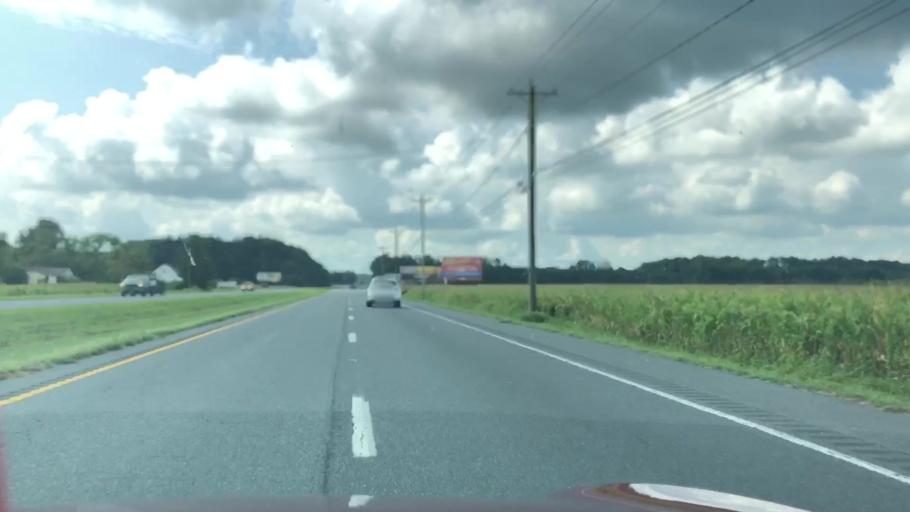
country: US
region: Virginia
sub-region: Accomack County
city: Wattsville
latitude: 37.9690
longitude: -75.5325
